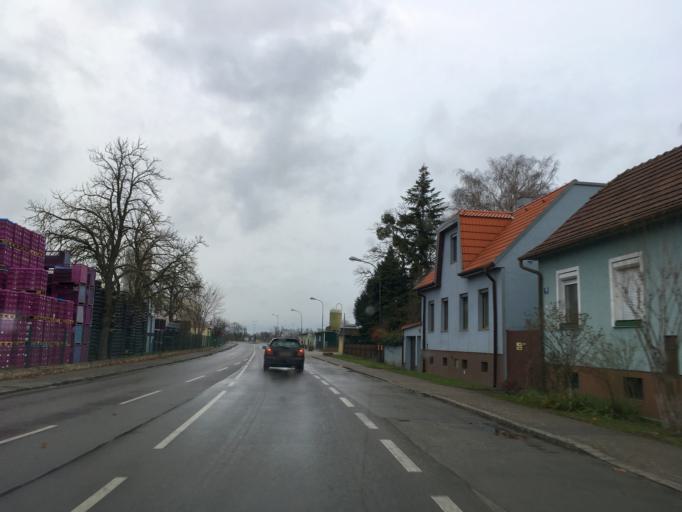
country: AT
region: Lower Austria
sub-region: Politischer Bezirk Wien-Umgebung
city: Ebergassing
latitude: 48.0436
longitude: 16.5216
